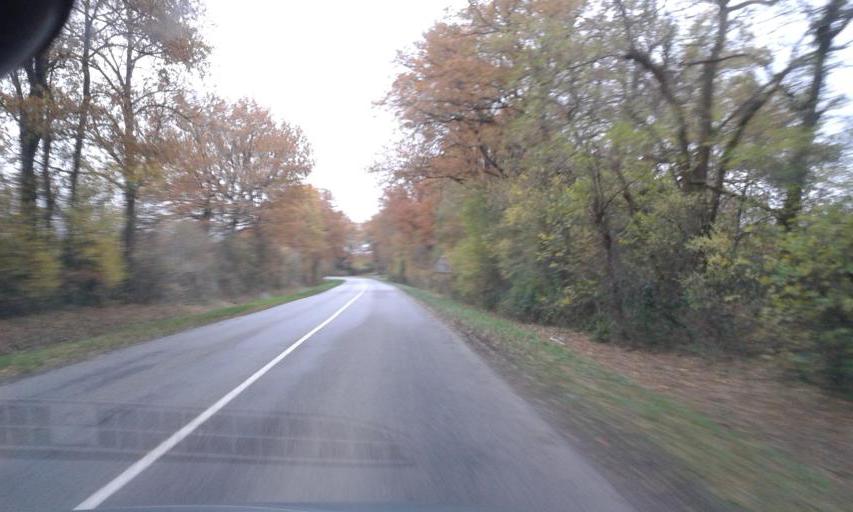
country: FR
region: Centre
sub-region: Departement du Loiret
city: Chateauneuf-sur-Loire
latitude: 47.8876
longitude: 2.2366
